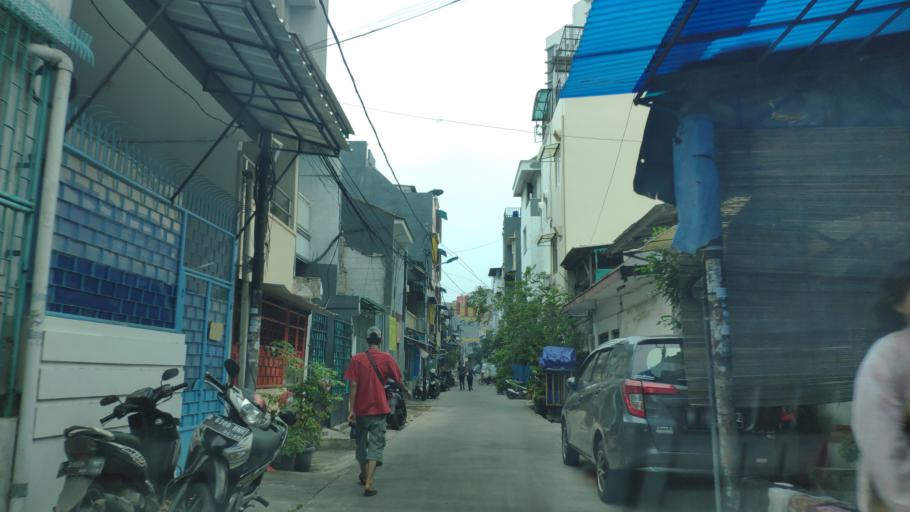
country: ID
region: Jakarta Raya
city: Jakarta
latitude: -6.1441
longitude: 106.8134
